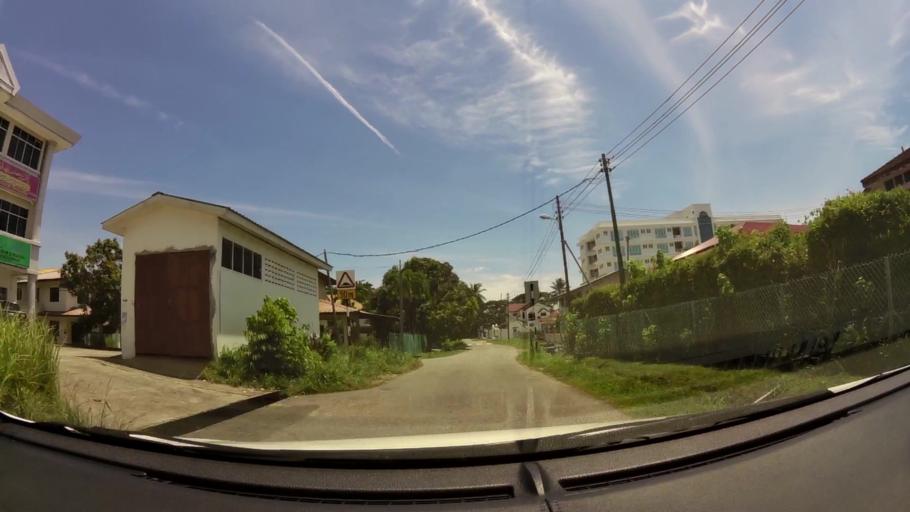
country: BN
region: Brunei and Muara
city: Bandar Seri Begawan
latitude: 4.9342
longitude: 114.9454
